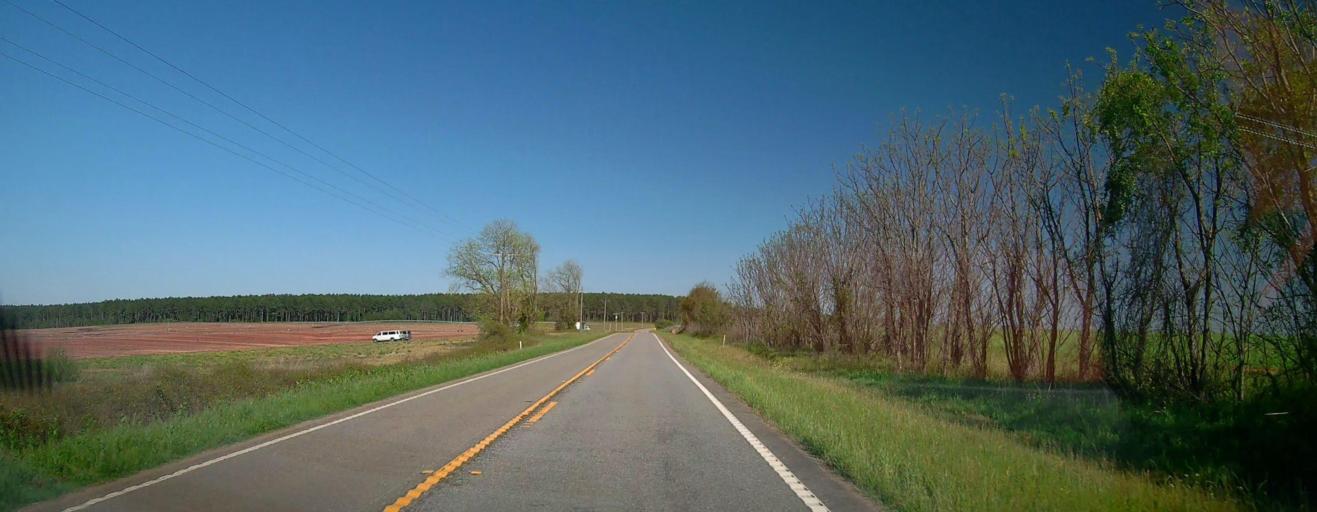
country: US
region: Georgia
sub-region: Dooly County
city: Unadilla
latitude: 32.2598
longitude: -83.6587
